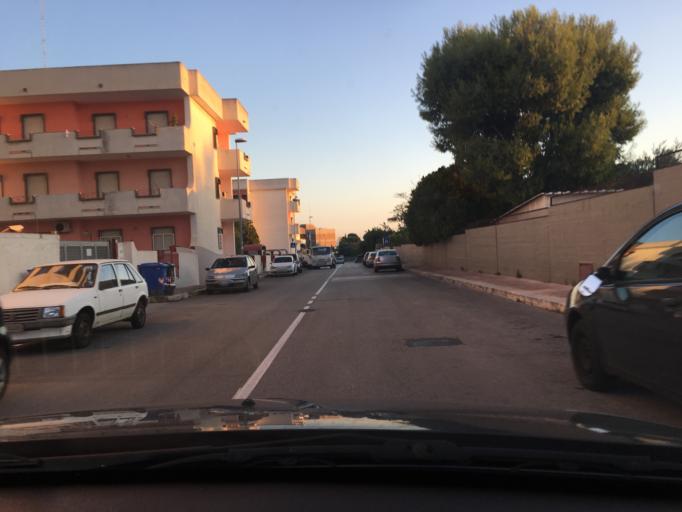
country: IT
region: Apulia
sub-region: Provincia di Bari
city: San Paolo
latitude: 41.1583
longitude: 16.7527
